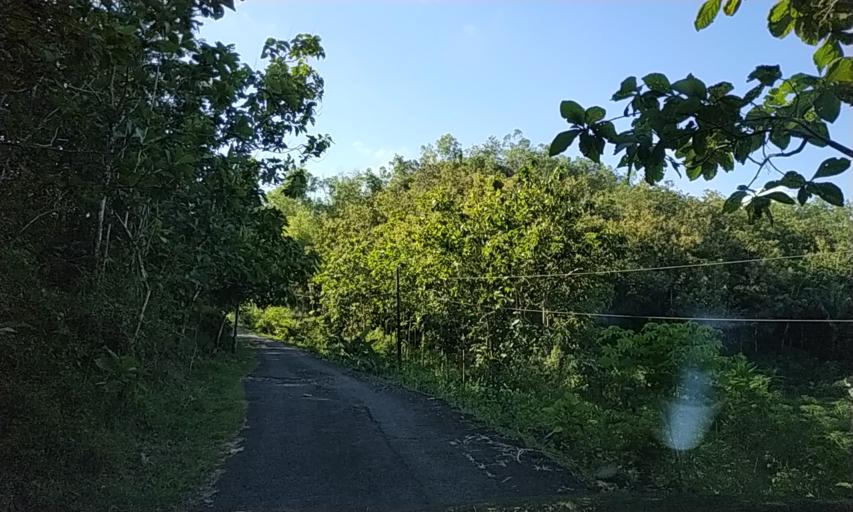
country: ID
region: East Java
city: Krajan
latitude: -8.1321
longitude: 110.9036
